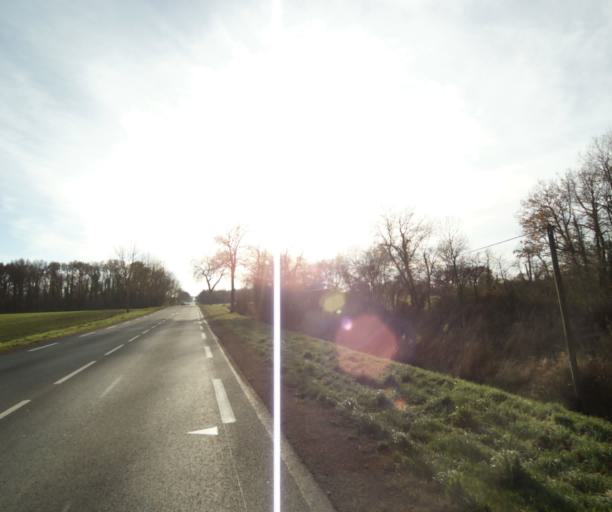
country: FR
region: Poitou-Charentes
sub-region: Departement de la Charente-Maritime
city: Saint-Hilaire-de-Villefranche
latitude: 45.8369
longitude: -0.5371
